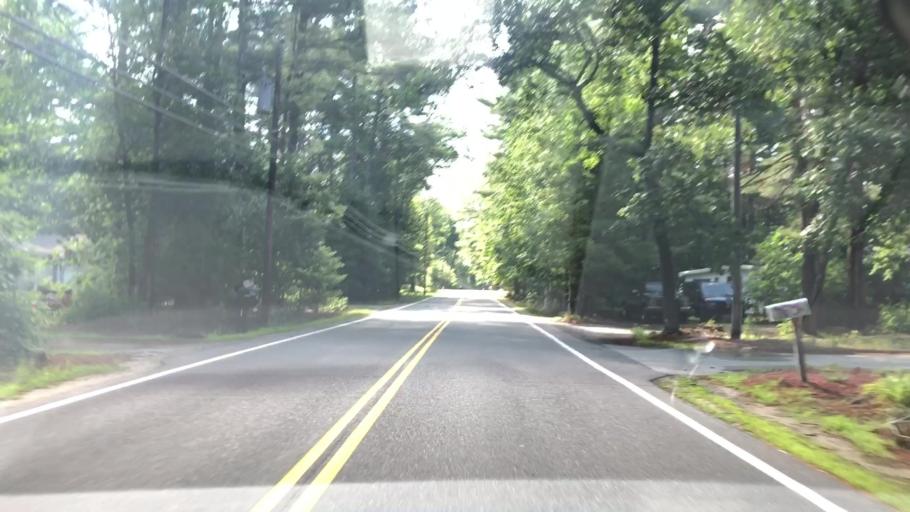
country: US
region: New Hampshire
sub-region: Hillsborough County
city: Milford
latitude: 42.8369
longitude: -71.5971
